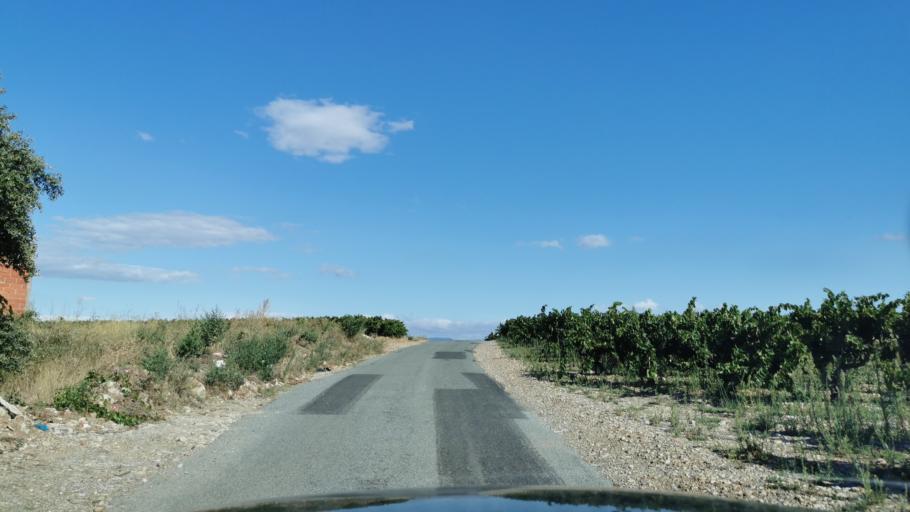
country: FR
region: Languedoc-Roussillon
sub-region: Departement de l'Aude
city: Ginestas
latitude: 43.2599
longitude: 2.8461
